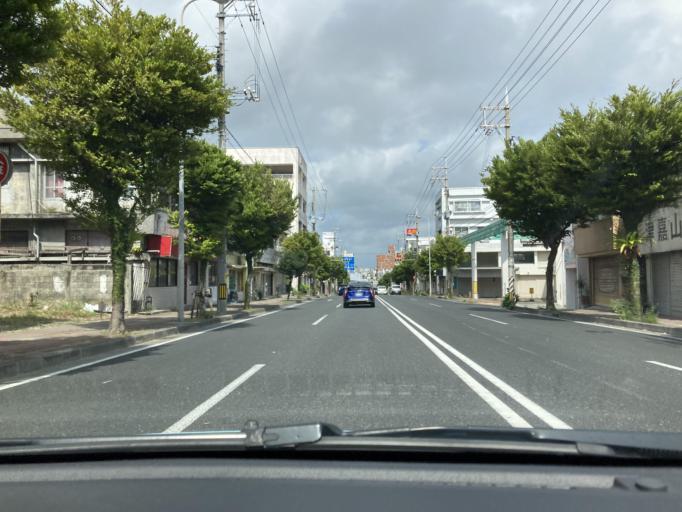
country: JP
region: Okinawa
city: Okinawa
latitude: 26.3361
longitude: 127.8172
